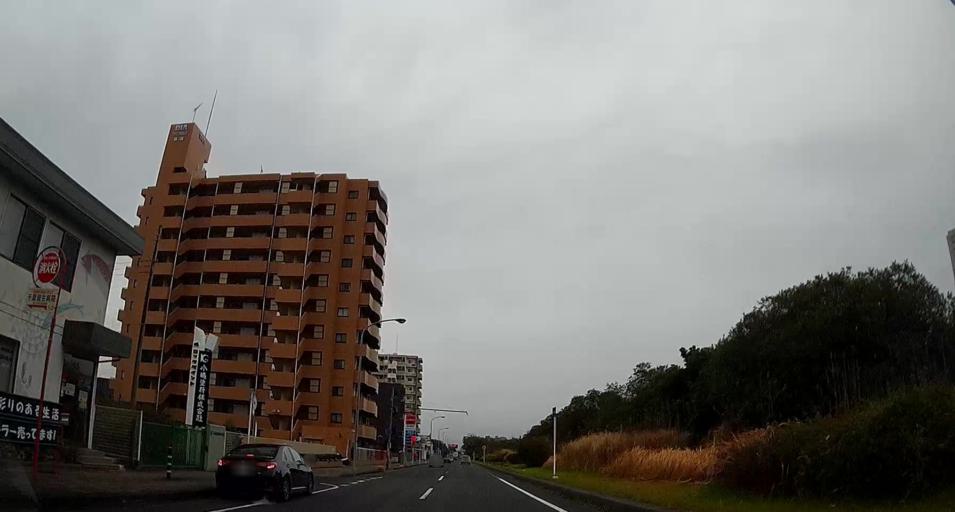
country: JP
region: Chiba
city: Chiba
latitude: 35.6538
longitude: 140.0572
